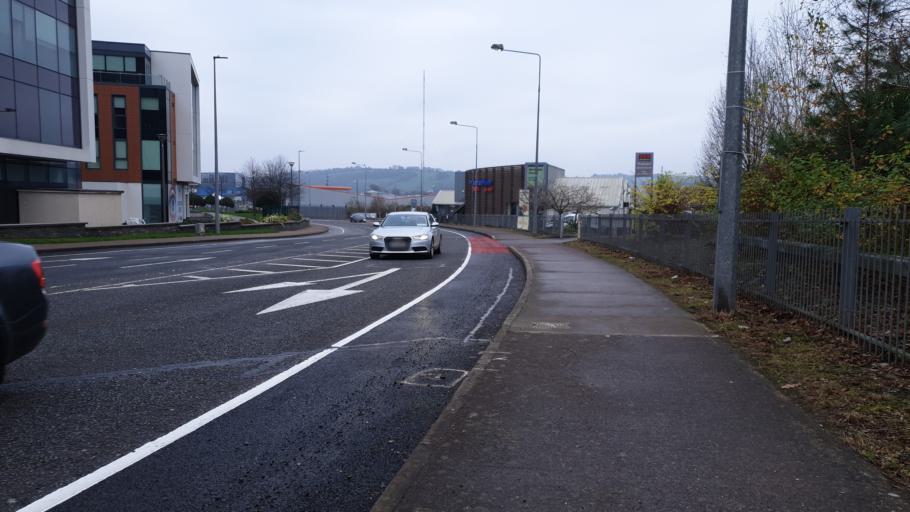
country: IE
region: Munster
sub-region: County Cork
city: Passage West
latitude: 51.8861
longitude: -8.4067
